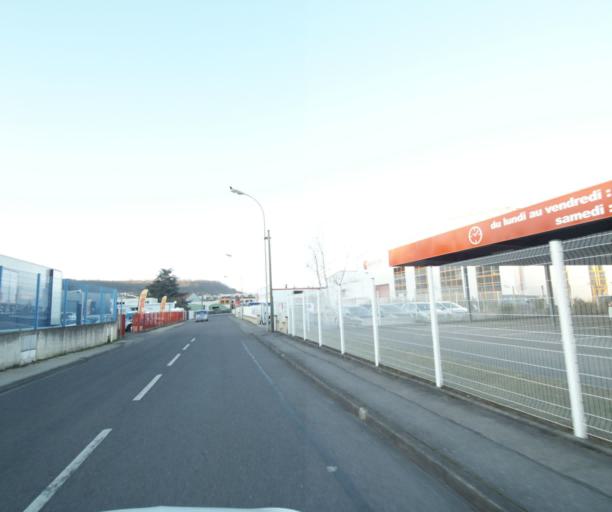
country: FR
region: Lorraine
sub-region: Departement de Meurthe-et-Moselle
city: Maxeville
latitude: 48.7085
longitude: 6.1687
